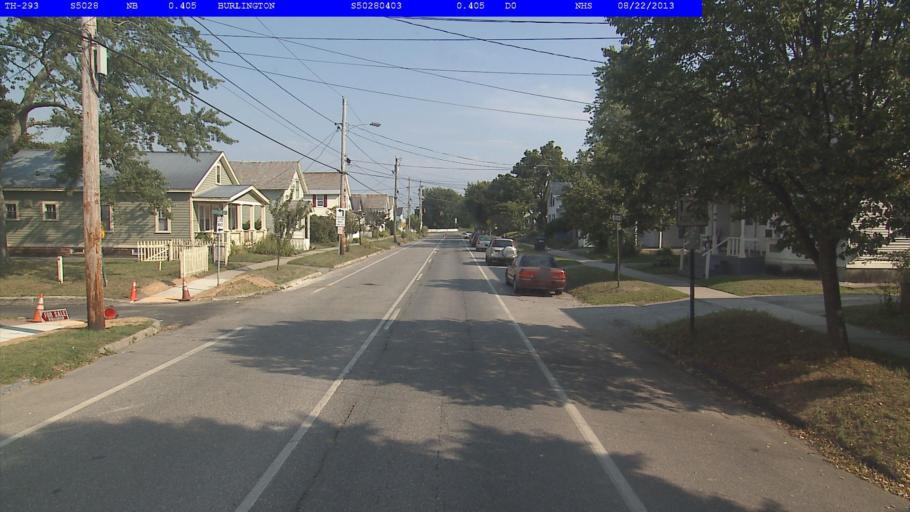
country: US
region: Vermont
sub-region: Chittenden County
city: Burlington
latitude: 44.4862
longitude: -73.2178
